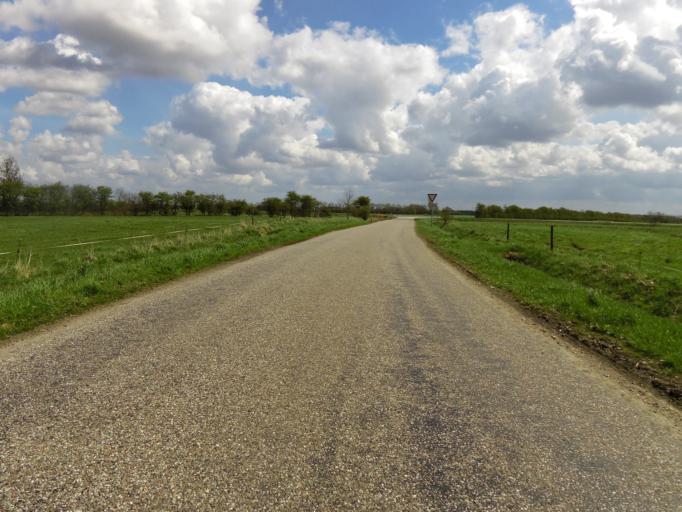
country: DK
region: South Denmark
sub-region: Tonder Kommune
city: Toftlund
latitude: 55.2097
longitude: 9.0912
